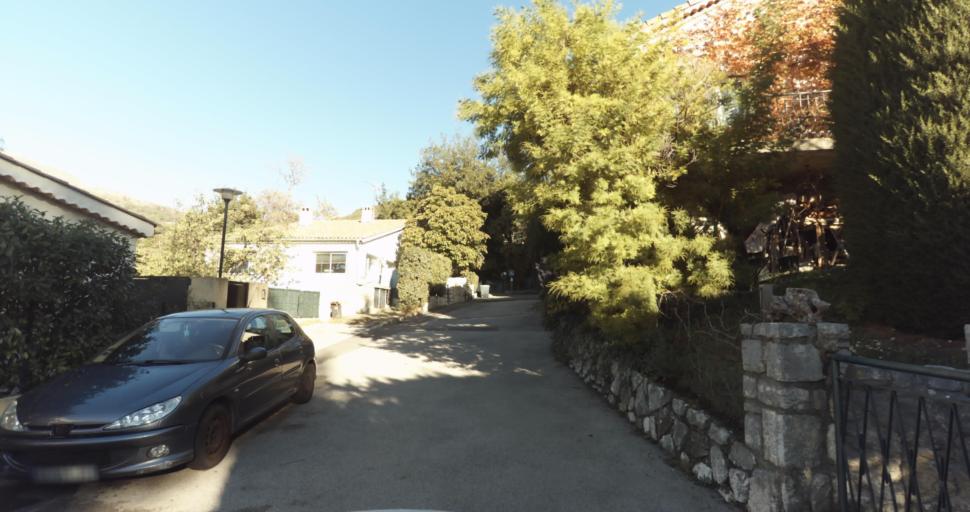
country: FR
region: Provence-Alpes-Cote d'Azur
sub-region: Departement des Alpes-Maritimes
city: Vence
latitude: 43.7244
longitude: 7.0953
